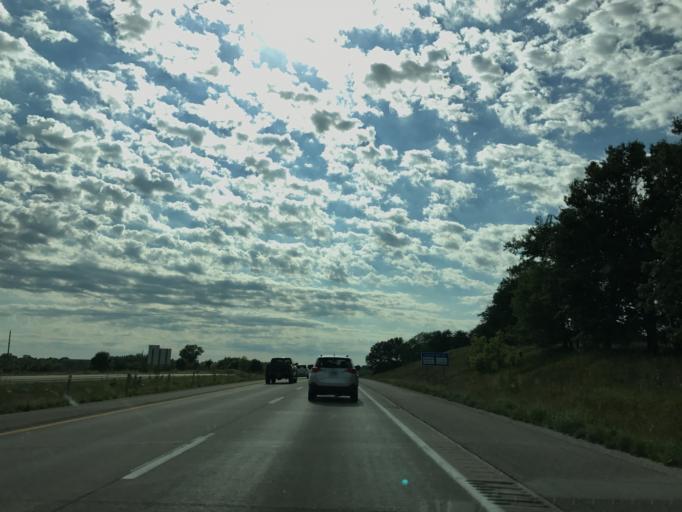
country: US
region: Iowa
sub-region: Dallas County
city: Van Meter
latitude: 41.5445
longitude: -93.9748
